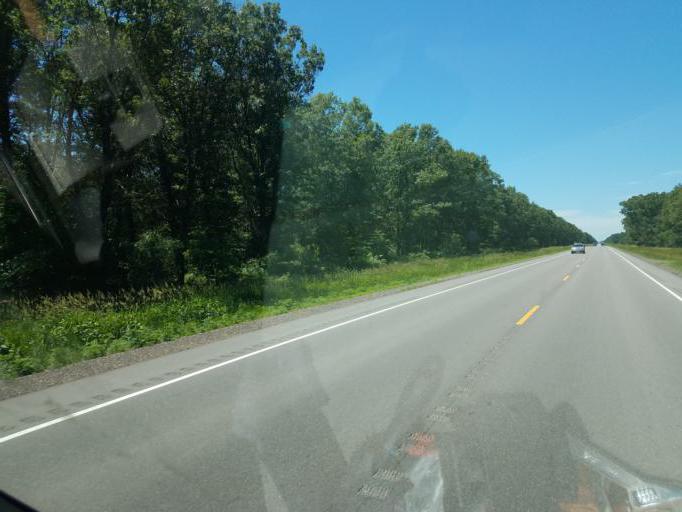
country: US
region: Wisconsin
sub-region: Juneau County
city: New Lisbon
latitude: 44.0256
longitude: -90.2188
